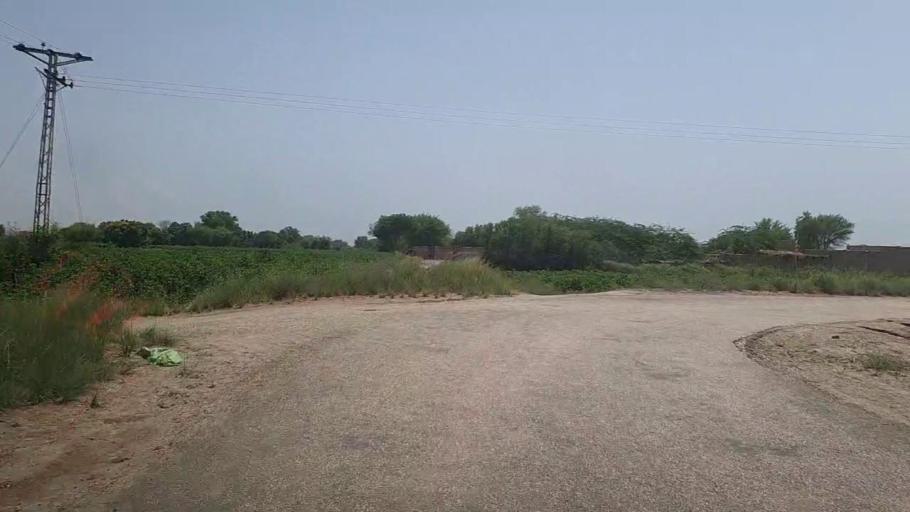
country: PK
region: Sindh
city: Pad Idan
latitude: 26.8345
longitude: 68.3248
